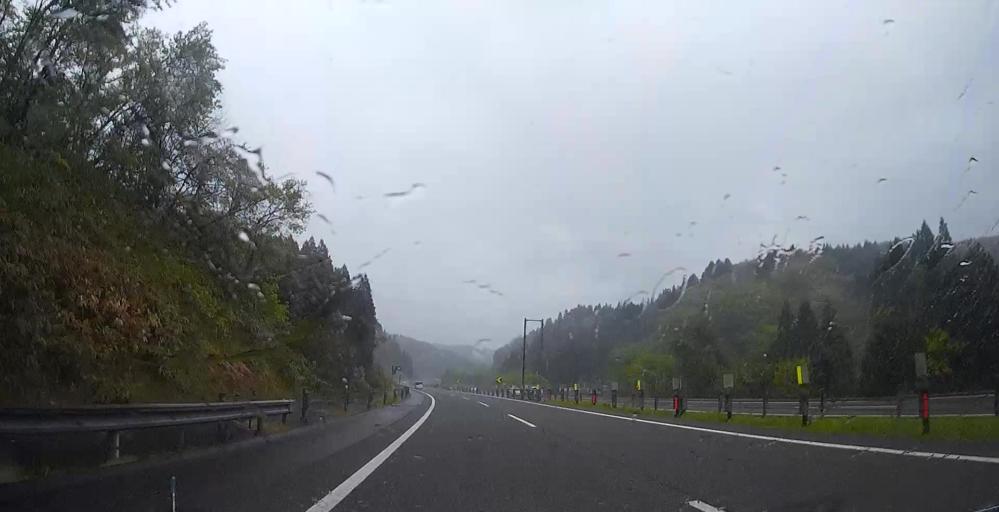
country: JP
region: Niigata
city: Nagaoka
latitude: 37.4348
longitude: 138.7065
